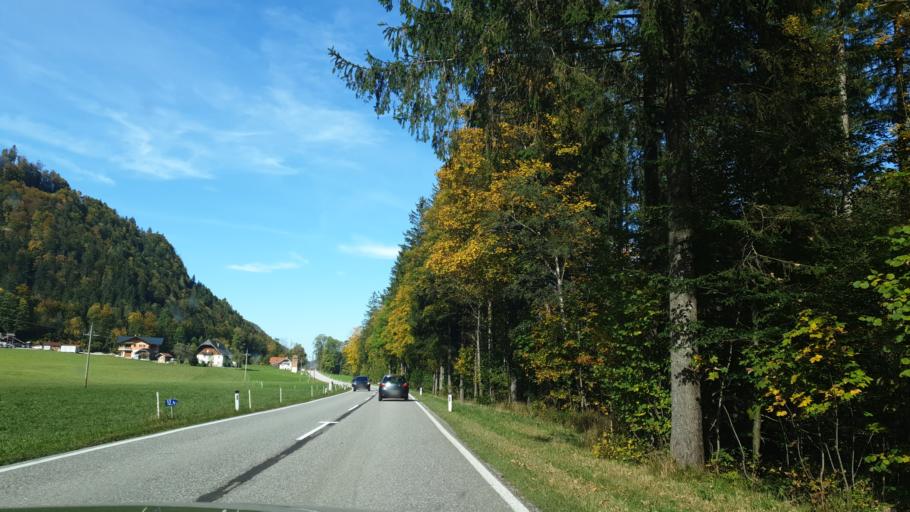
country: AT
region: Salzburg
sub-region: Politischer Bezirk Salzburg-Umgebung
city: Hintersee
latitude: 47.7227
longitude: 13.2784
